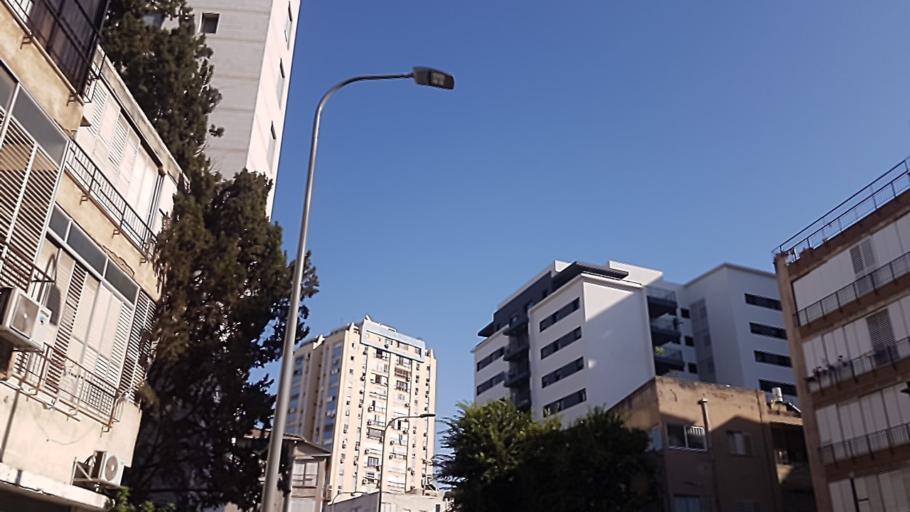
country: IL
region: Tel Aviv
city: Ramat Gan
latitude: 32.0797
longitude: 34.8132
